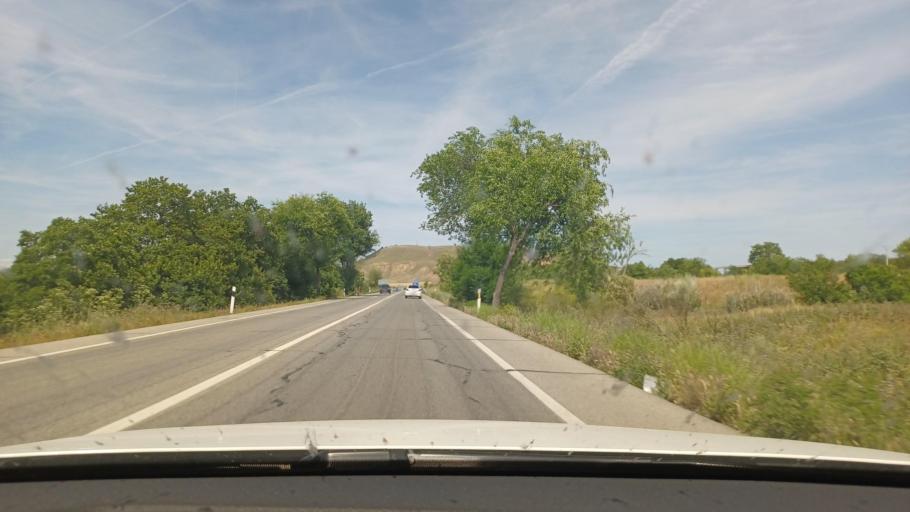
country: ES
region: Madrid
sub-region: Provincia de Madrid
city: Torrejon de Ardoz
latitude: 40.4369
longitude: -3.4334
